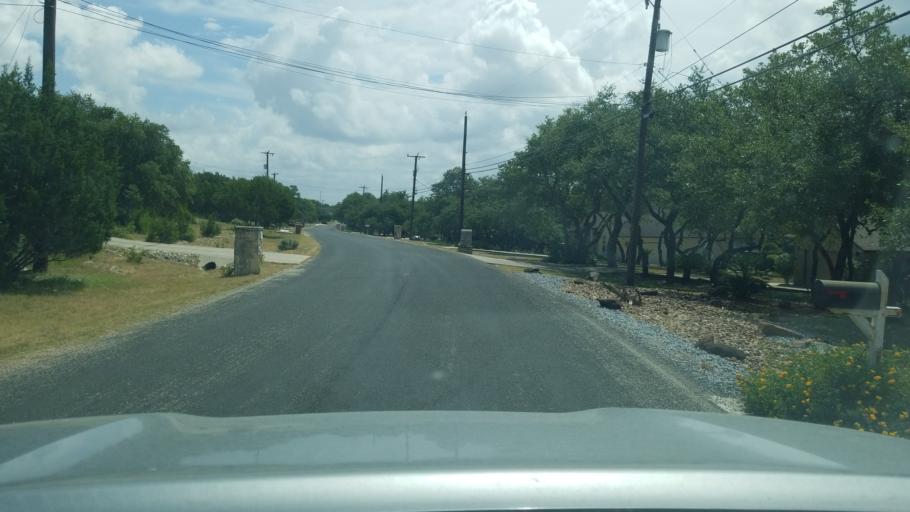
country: US
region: Texas
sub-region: Bexar County
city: Timberwood Park
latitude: 29.6992
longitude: -98.4980
